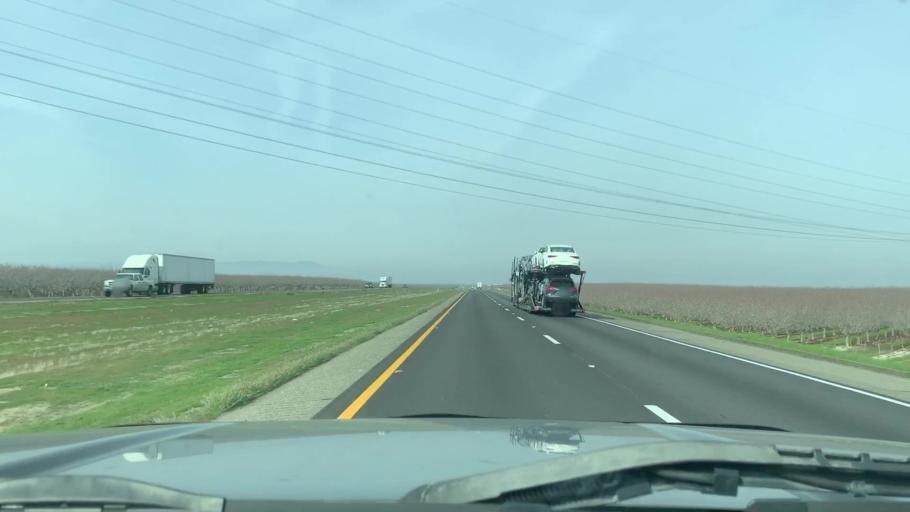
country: US
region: California
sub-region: Fresno County
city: Huron
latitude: 36.1108
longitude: -120.1341
